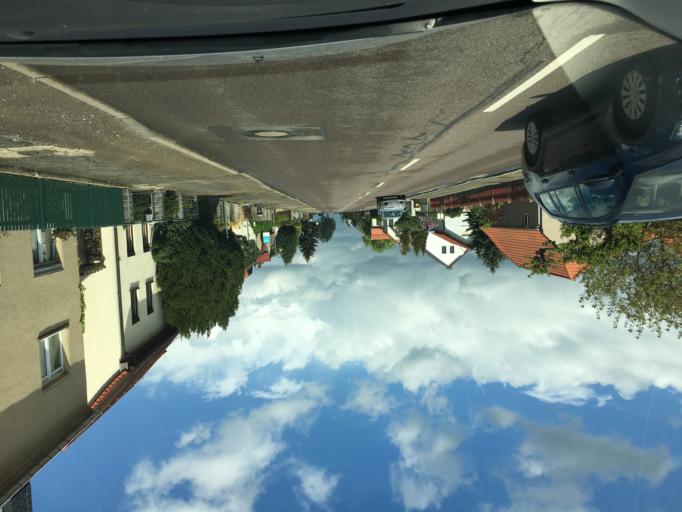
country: DE
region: Saxony
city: Borna
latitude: 51.1055
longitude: 12.5129
